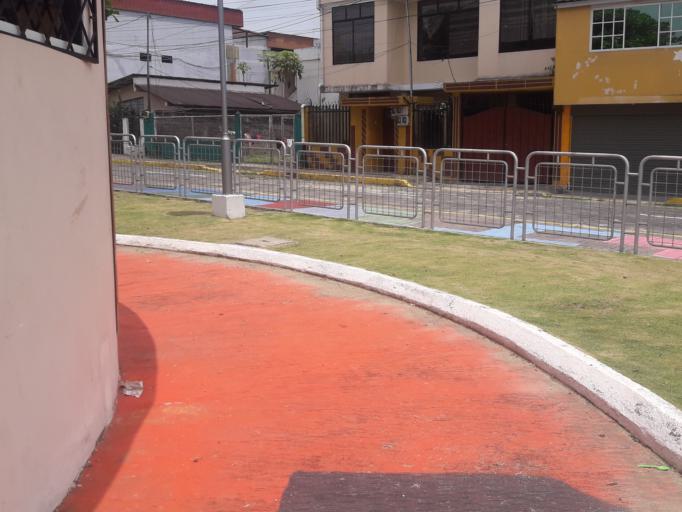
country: EC
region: Napo
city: Tena
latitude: -0.9932
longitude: -77.8119
